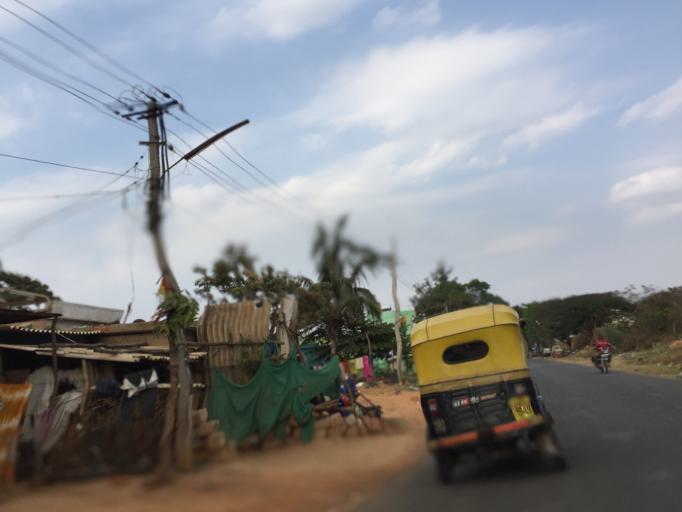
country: IN
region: Karnataka
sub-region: Chikkaballapur
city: Chik Ballapur
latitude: 13.4136
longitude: 77.7173
